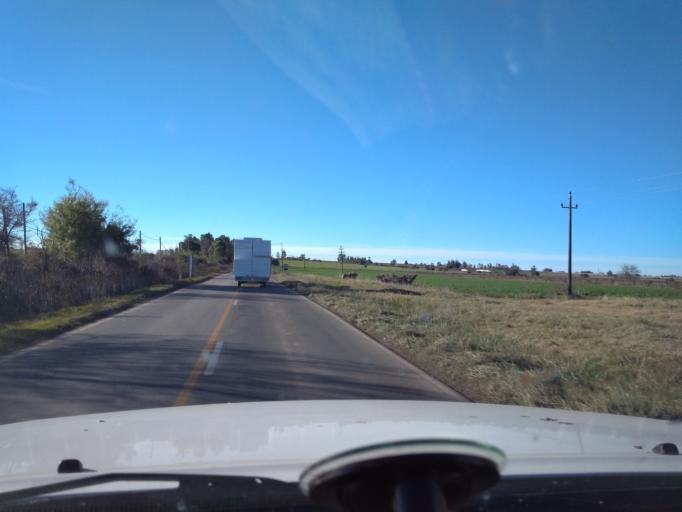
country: UY
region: Canelones
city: Santa Rosa
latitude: -34.4718
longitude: -56.0077
